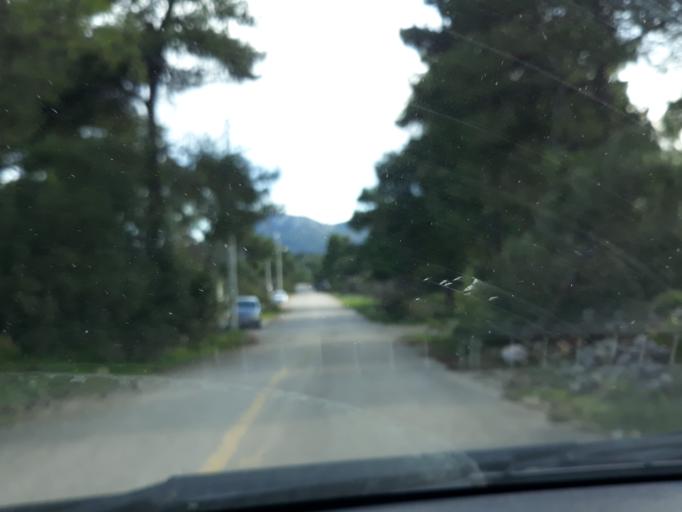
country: GR
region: Attica
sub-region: Nomarchia Anatolikis Attikis
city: Afidnes
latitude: 38.2166
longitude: 23.7984
